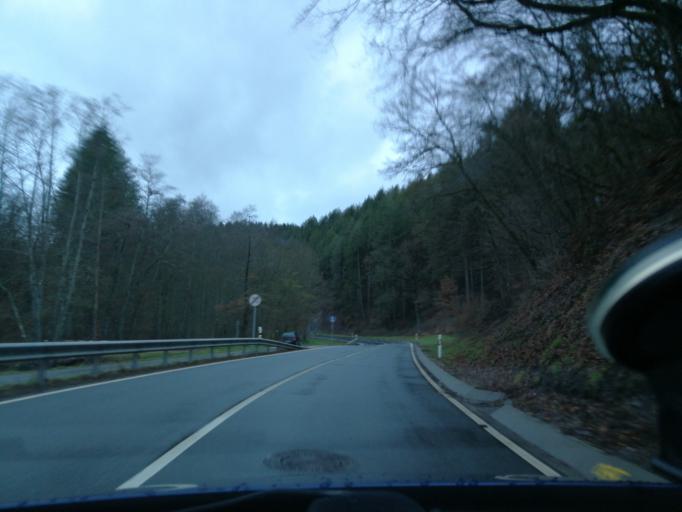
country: DE
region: Rheinland-Pfalz
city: Bruch
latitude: 49.9565
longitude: 6.7760
